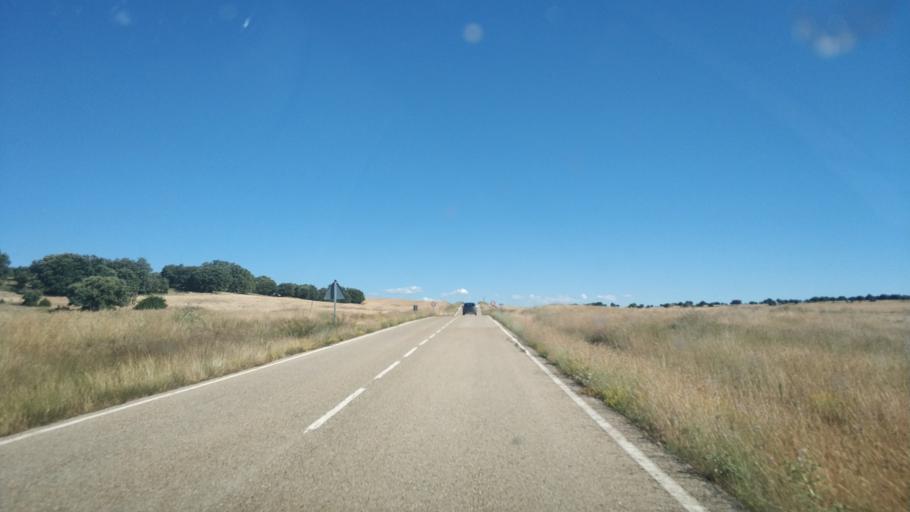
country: ES
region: Castille and Leon
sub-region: Provincia de Soria
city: Montejo de Tiermes
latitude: 41.3957
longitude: -3.1989
